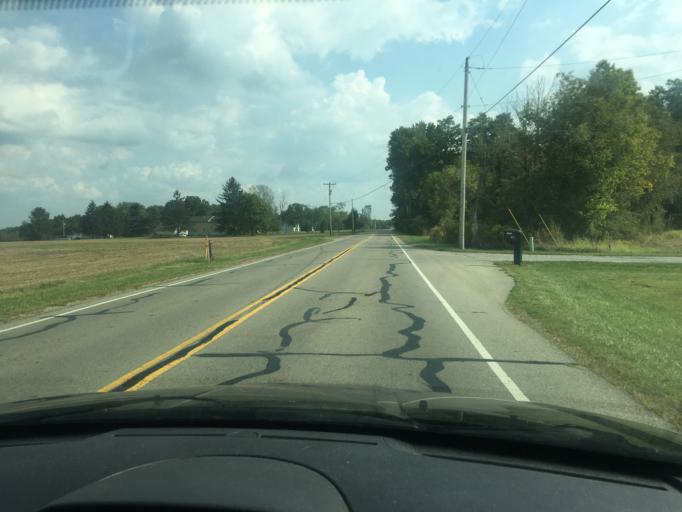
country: US
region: Ohio
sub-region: Champaign County
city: Urbana
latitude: 40.1260
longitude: -83.7695
